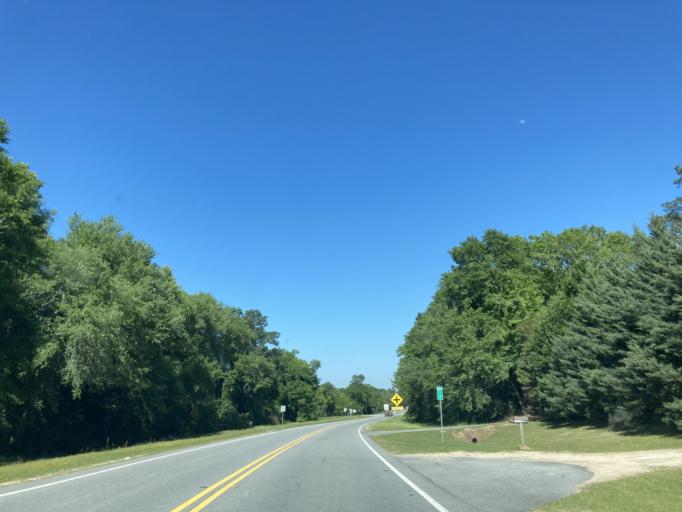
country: US
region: Georgia
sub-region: Baker County
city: Newton
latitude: 31.3277
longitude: -84.3369
